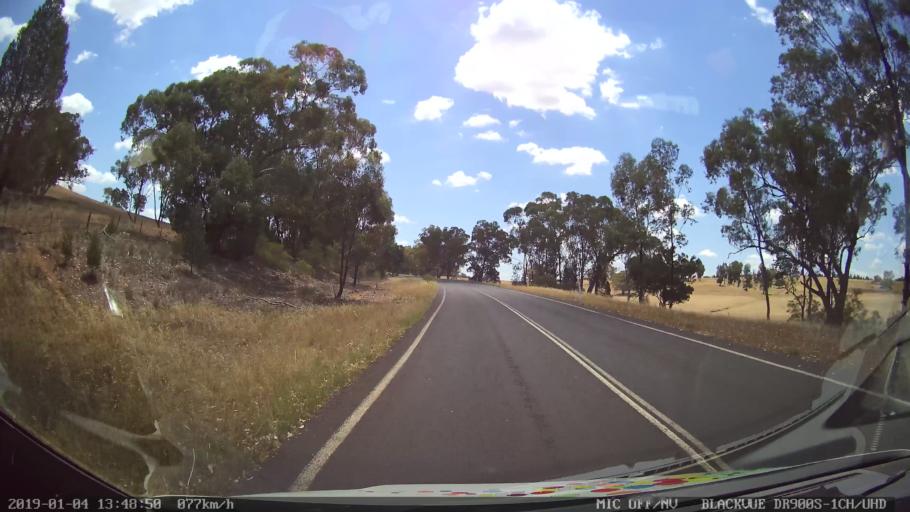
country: AU
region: New South Wales
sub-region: Dubbo Municipality
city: Dubbo
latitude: -32.4379
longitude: 148.5840
